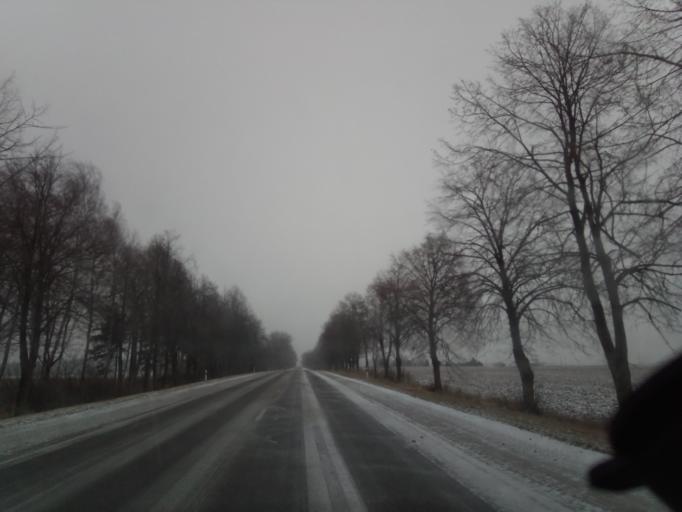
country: LT
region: Vilnius County
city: Ukmerge
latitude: 55.3500
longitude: 24.9435
